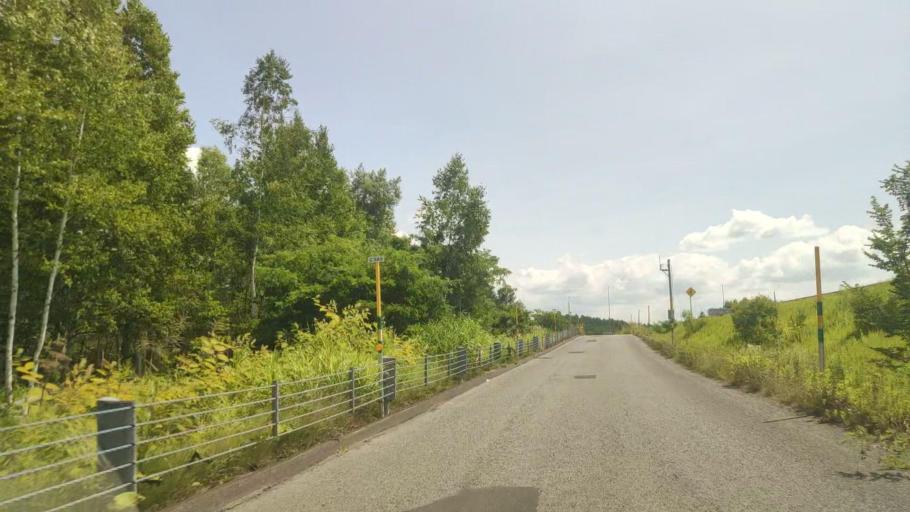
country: JP
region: Hokkaido
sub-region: Asahikawa-shi
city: Asahikawa
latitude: 43.9194
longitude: 142.4994
